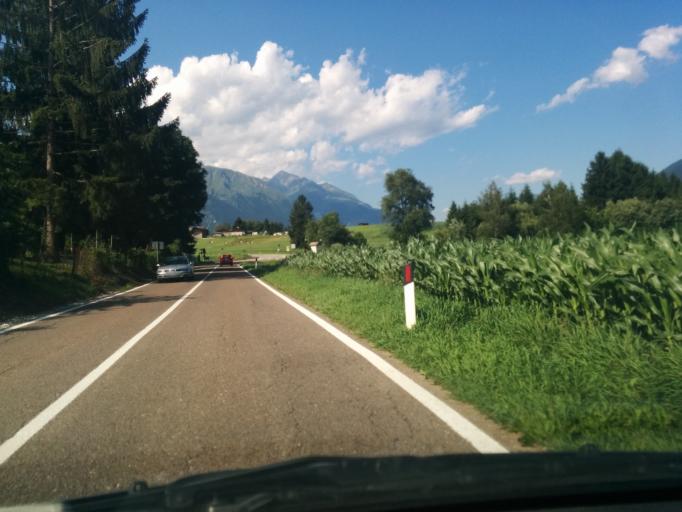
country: IT
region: Trentino-Alto Adige
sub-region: Provincia di Trento
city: Fiave
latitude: 45.9945
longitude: 10.8400
